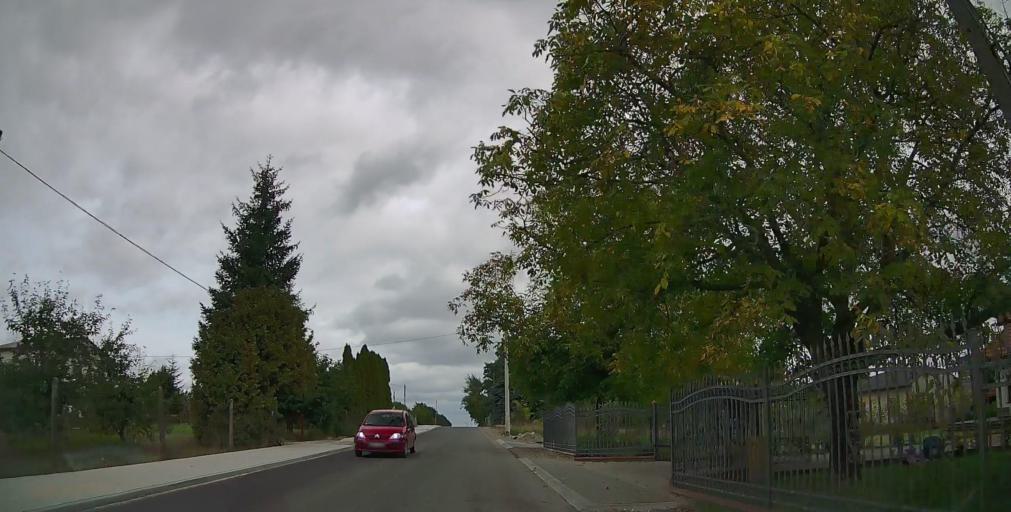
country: PL
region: Masovian Voivodeship
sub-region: Powiat grojecki
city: Belsk Duzy
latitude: 51.8146
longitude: 20.8299
